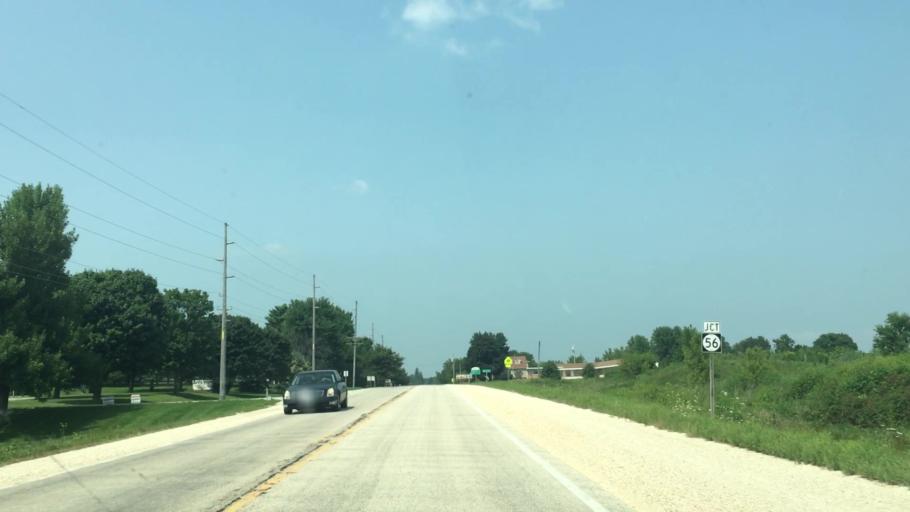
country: US
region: Iowa
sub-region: Fayette County
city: West Union
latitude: 42.9480
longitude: -91.8142
